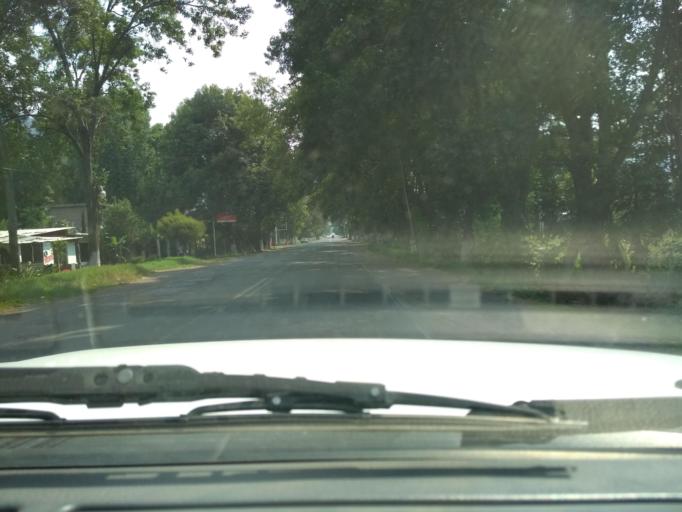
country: MX
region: Veracruz
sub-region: Acultzingo
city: Sierra de Agua
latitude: 18.7568
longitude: -97.2323
